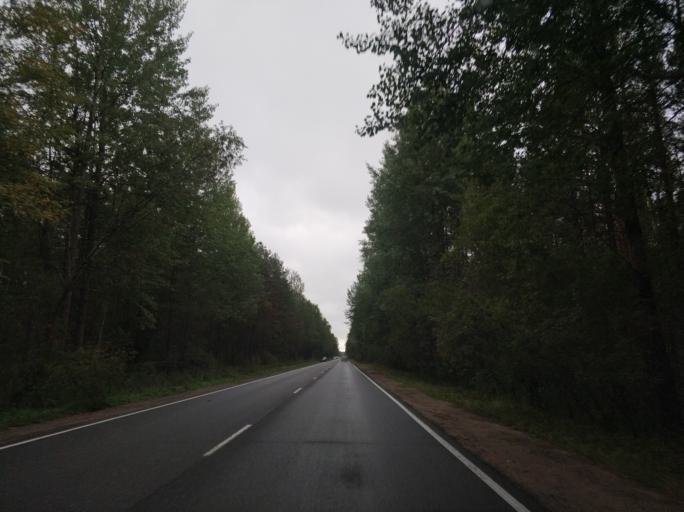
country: RU
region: Leningrad
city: Borisova Griva
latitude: 60.1499
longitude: 30.9384
